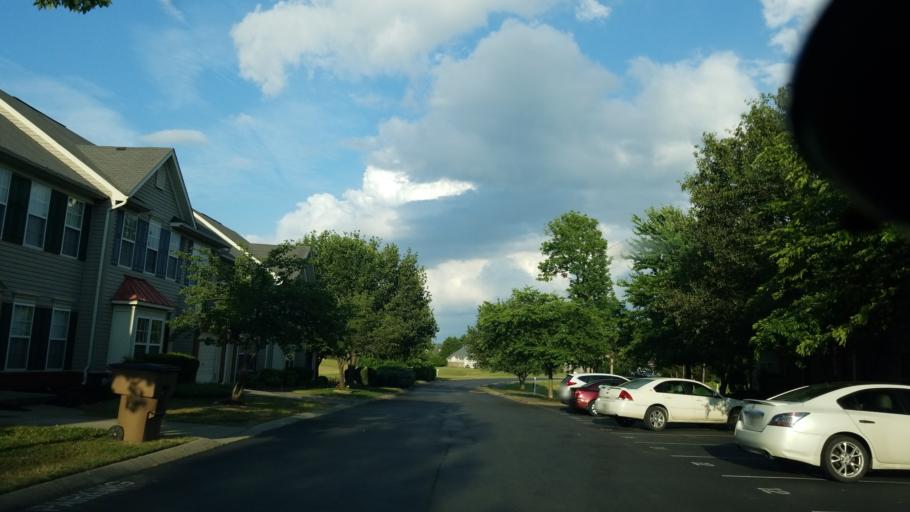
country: US
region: Tennessee
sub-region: Rutherford County
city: La Vergne
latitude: 36.0844
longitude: -86.6048
